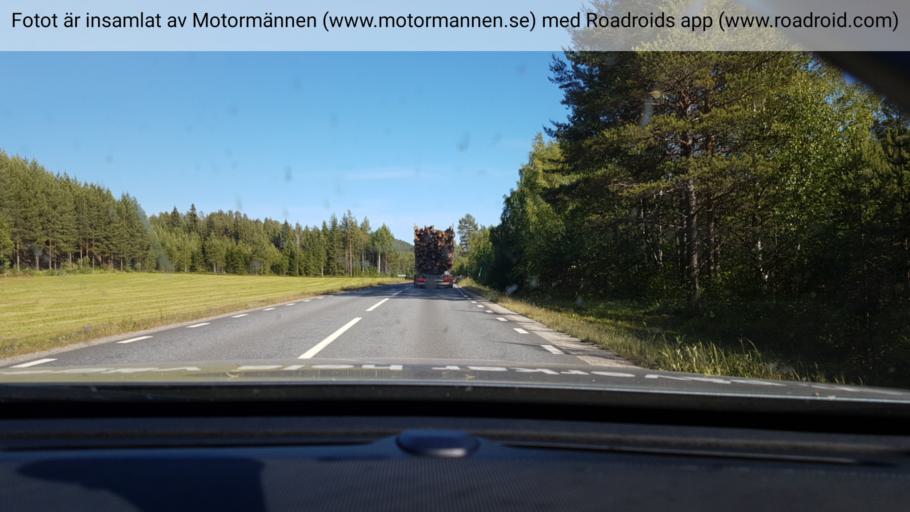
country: SE
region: Vaesterbotten
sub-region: Bjurholms Kommun
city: Bjurholm
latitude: 64.2804
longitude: 19.2420
